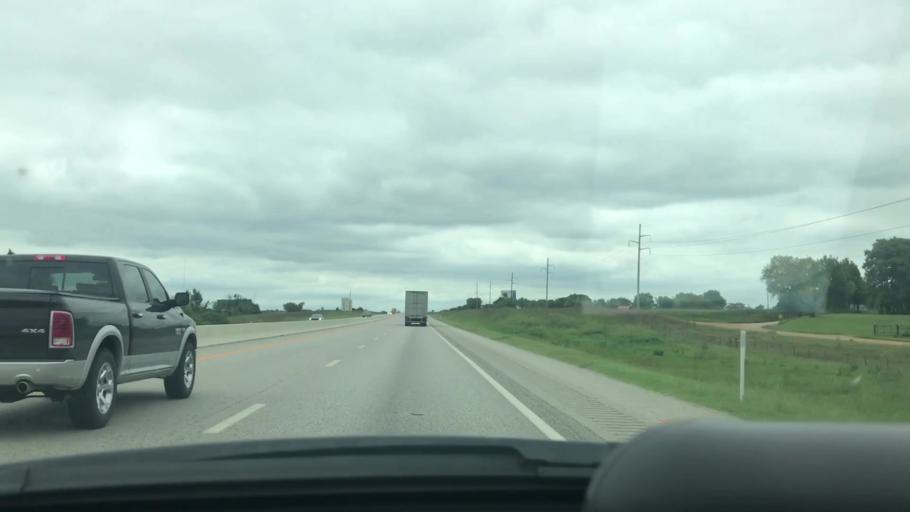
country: US
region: Oklahoma
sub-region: Craig County
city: Vinita
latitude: 36.6404
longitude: -95.1210
